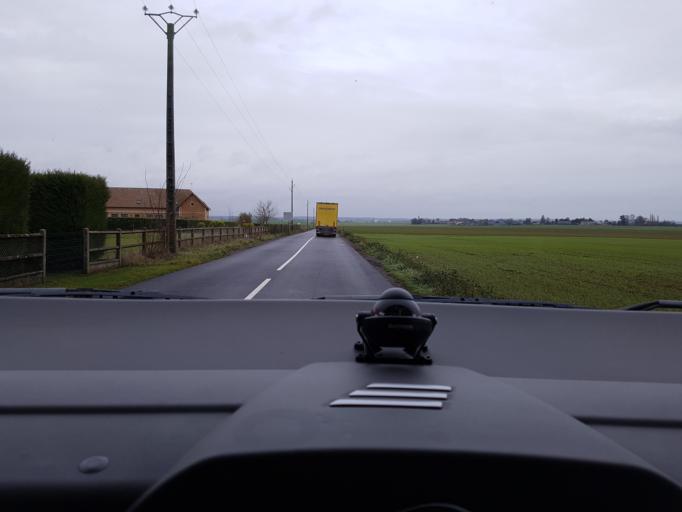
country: FR
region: Haute-Normandie
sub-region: Departement de l'Eure
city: Etrepagny
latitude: 49.3611
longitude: 1.5559
